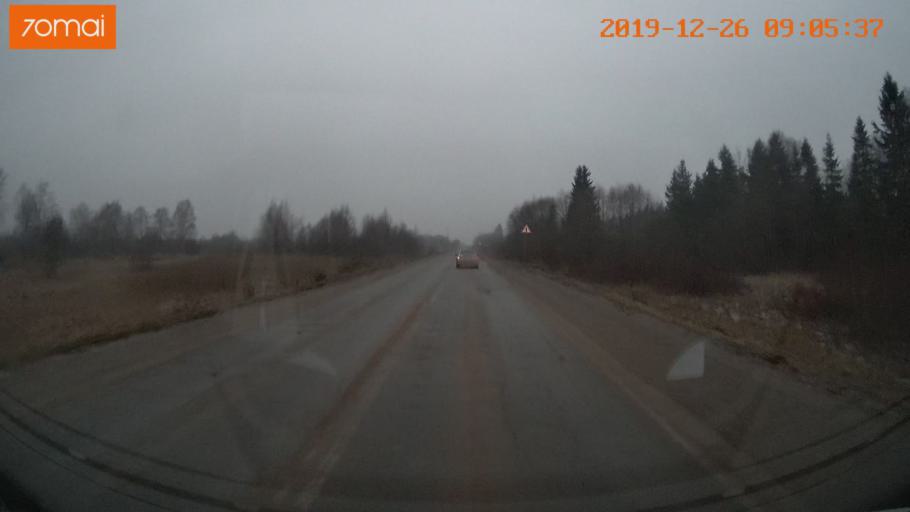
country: RU
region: Vologda
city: Gryazovets
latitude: 58.8274
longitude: 40.2572
